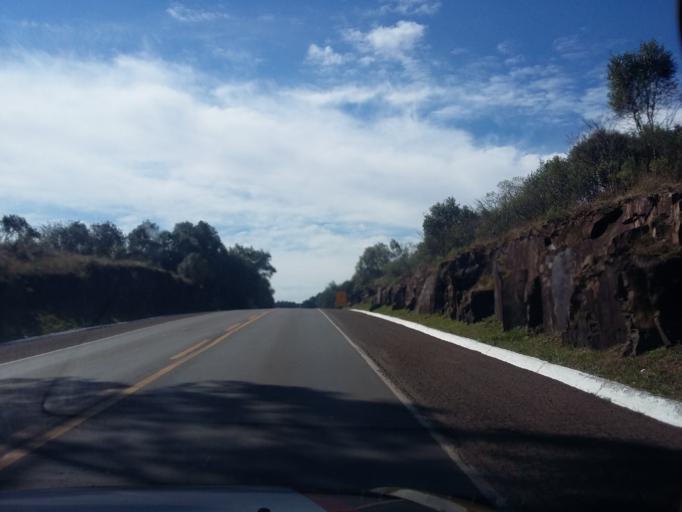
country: BR
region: Rio Grande do Sul
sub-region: Vacaria
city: Vacaria
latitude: -28.5527
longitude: -50.9831
